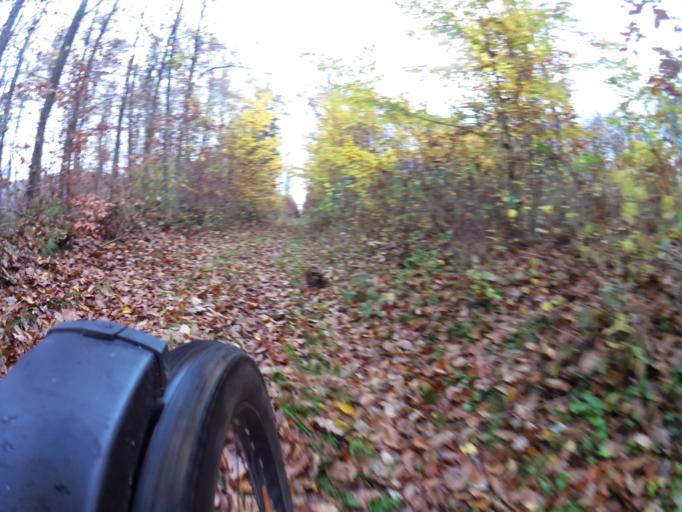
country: PL
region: Pomeranian Voivodeship
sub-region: Powiat pucki
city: Krokowa
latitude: 54.7314
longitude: 18.1320
